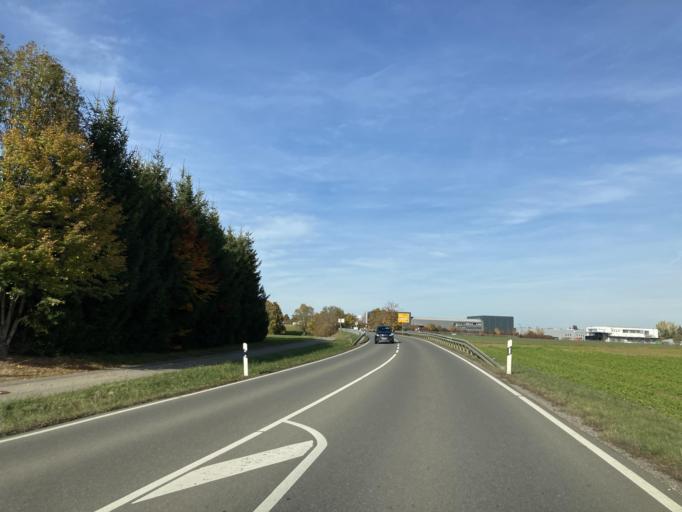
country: DE
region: Baden-Wuerttemberg
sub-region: Tuebingen Region
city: Bodelshausen
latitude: 48.3785
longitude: 8.9601
